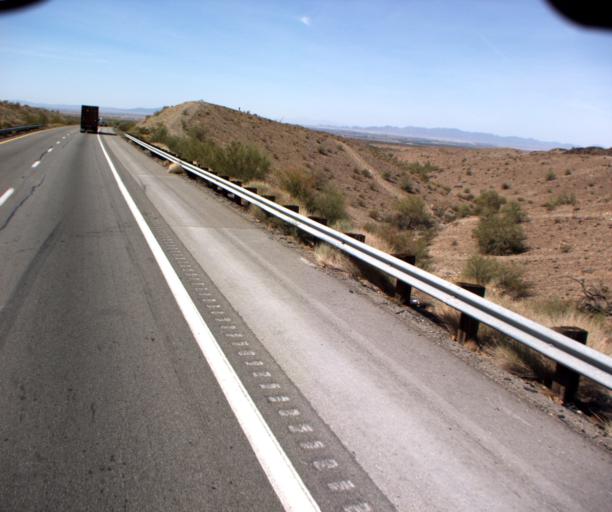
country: US
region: Arizona
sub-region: La Paz County
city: Ehrenberg
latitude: 33.6328
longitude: -114.4039
